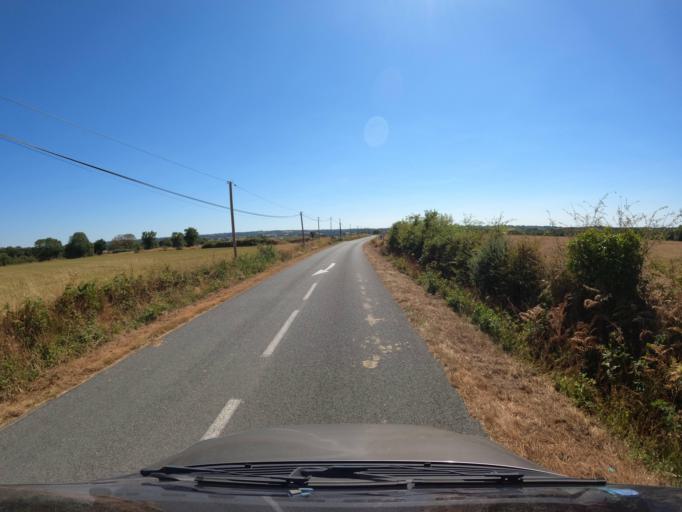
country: FR
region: Pays de la Loire
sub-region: Departement de la Vendee
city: Saint-Aubin-des-Ormeaux
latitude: 47.0133
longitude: -0.9979
